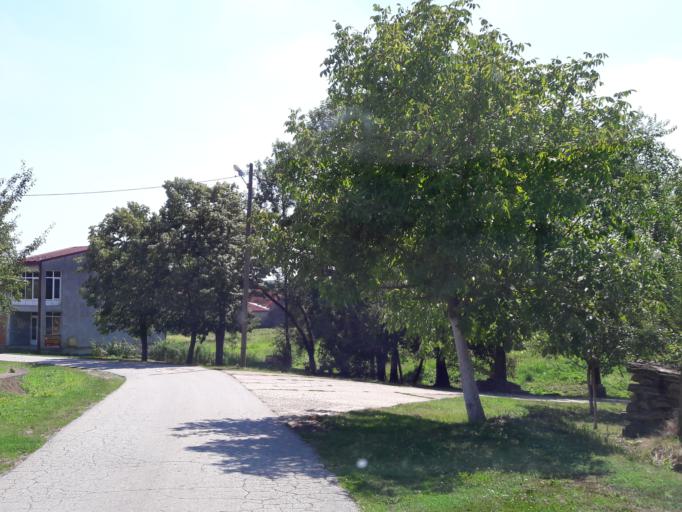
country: HR
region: Vukovarsko-Srijemska
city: Vodinci
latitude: 45.2847
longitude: 18.5609
